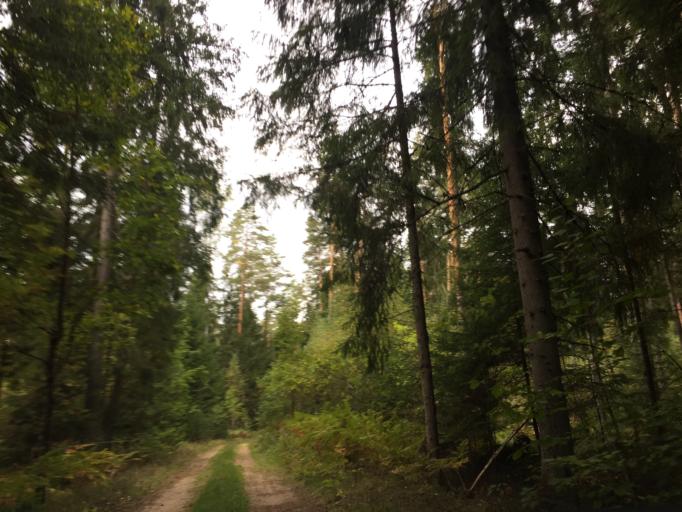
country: LV
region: Baldone
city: Baldone
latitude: 56.7761
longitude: 24.4439
